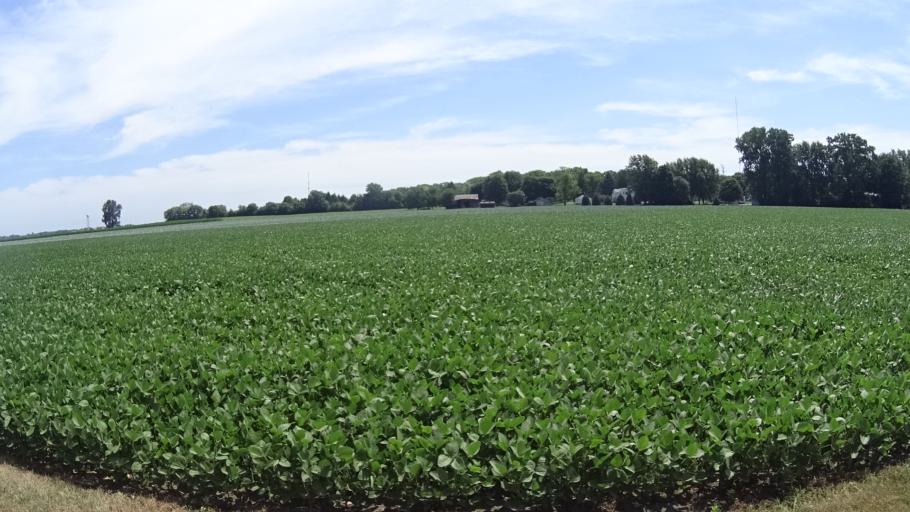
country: US
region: Ohio
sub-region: Erie County
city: Sandusky
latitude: 41.4028
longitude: -82.8046
